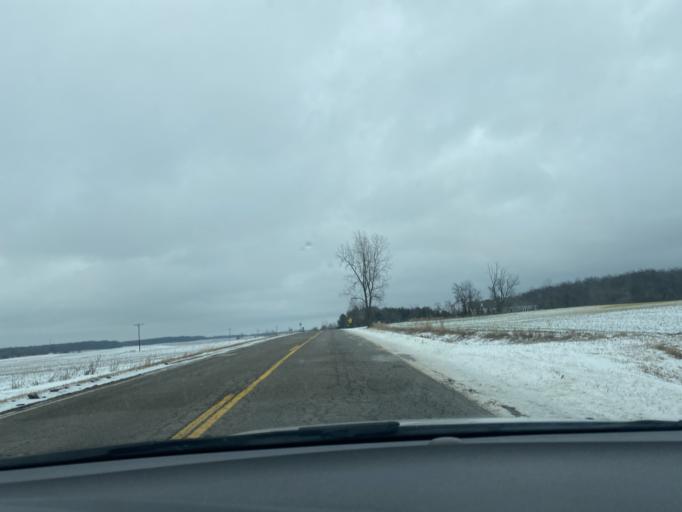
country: US
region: Michigan
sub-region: Lapeer County
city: North Branch
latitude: 43.2094
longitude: -83.1230
